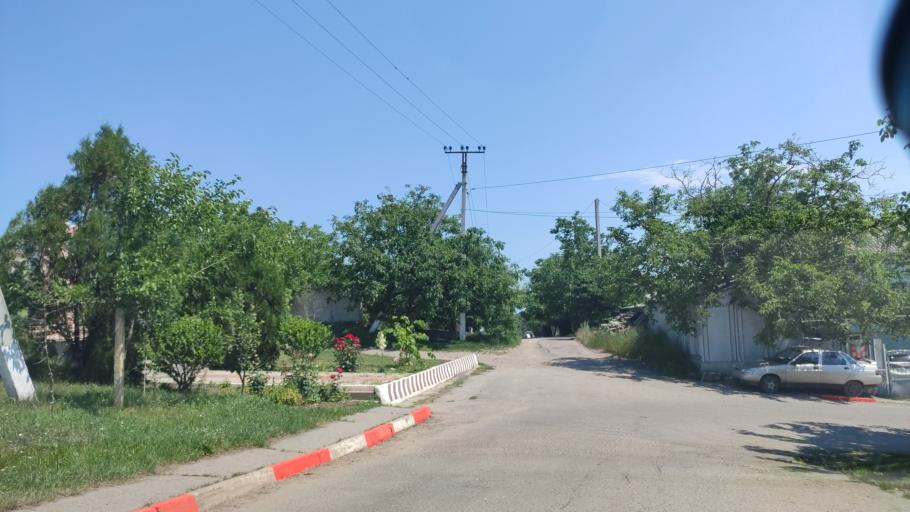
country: MD
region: Raionul Soroca
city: Soroca
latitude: 48.1726
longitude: 28.2952
